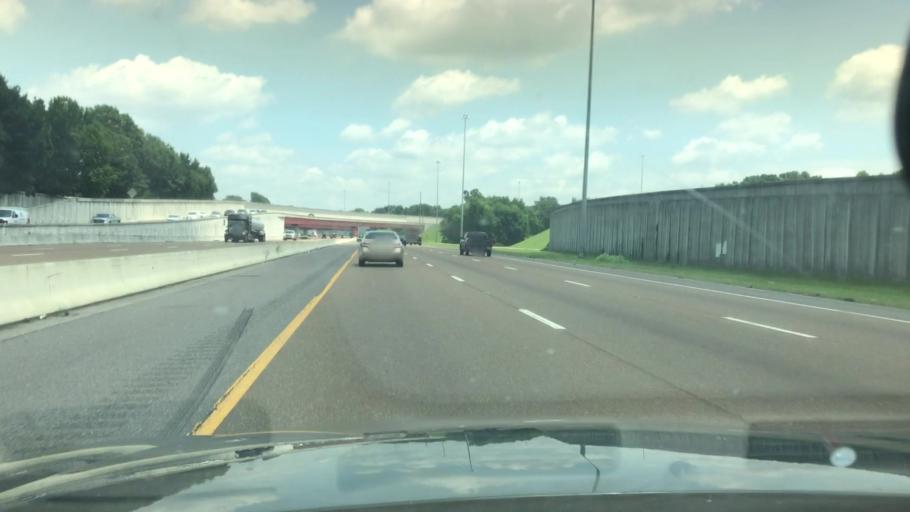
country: US
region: Tennessee
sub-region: Shelby County
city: Germantown
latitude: 35.0843
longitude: -89.8842
